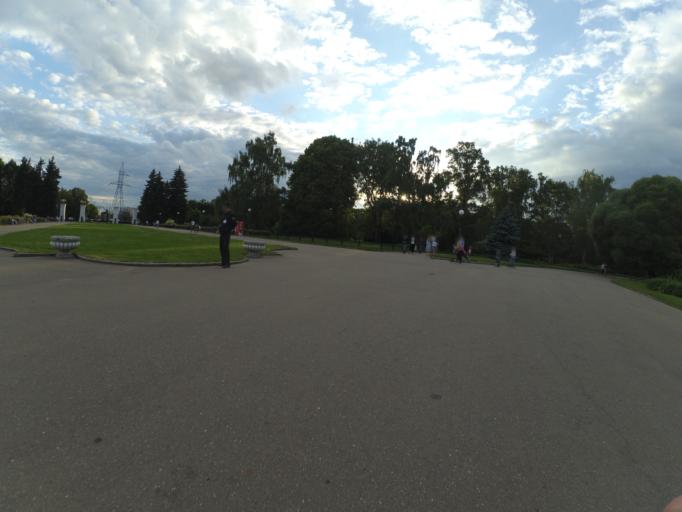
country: RU
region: Moscow
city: Novovladykino
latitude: 55.8432
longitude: 37.5892
